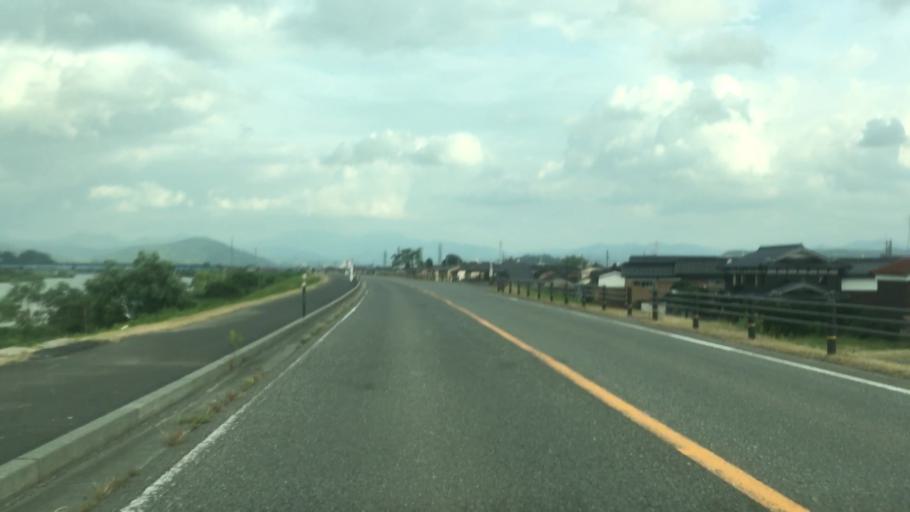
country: JP
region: Hyogo
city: Toyooka
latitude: 35.5634
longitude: 134.8126
